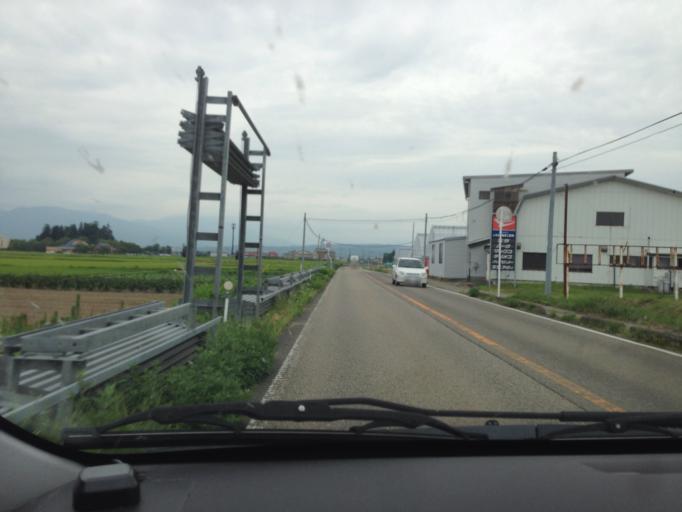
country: JP
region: Fukushima
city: Kitakata
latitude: 37.4945
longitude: 139.8638
